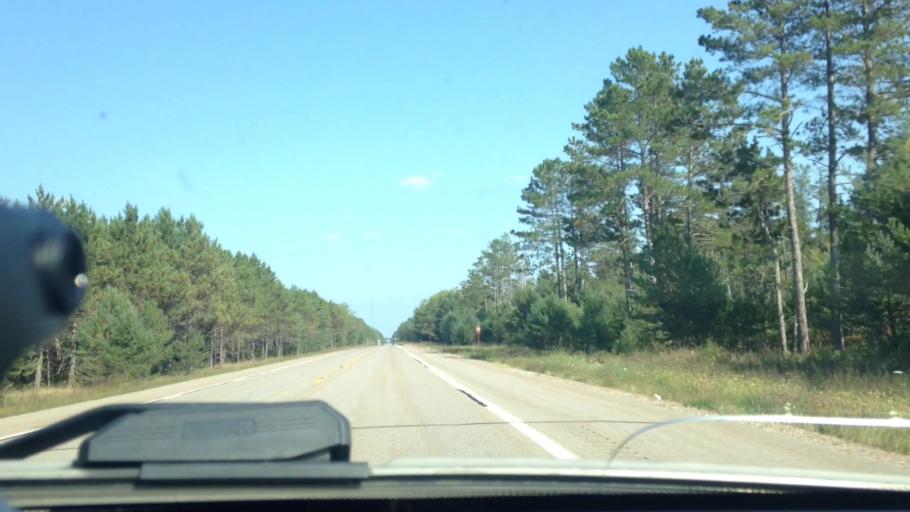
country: US
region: Michigan
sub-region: Chippewa County
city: Sault Ste. Marie
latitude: 46.3669
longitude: -84.7516
